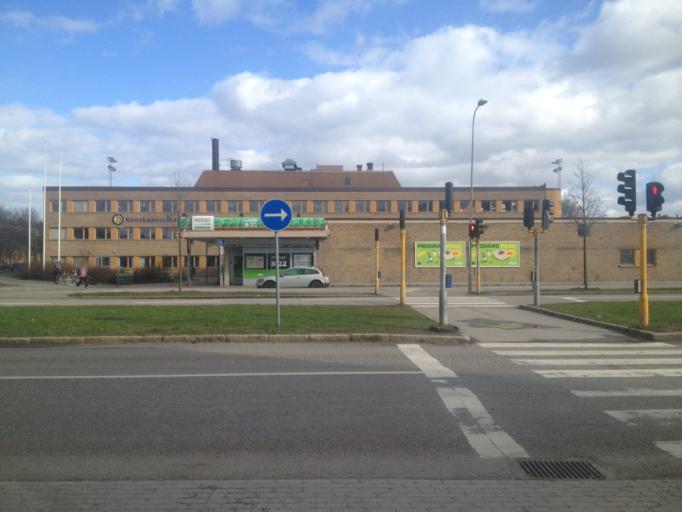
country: SE
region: Stockholm
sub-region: Stockholms Kommun
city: Arsta
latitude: 59.2830
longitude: 18.0717
